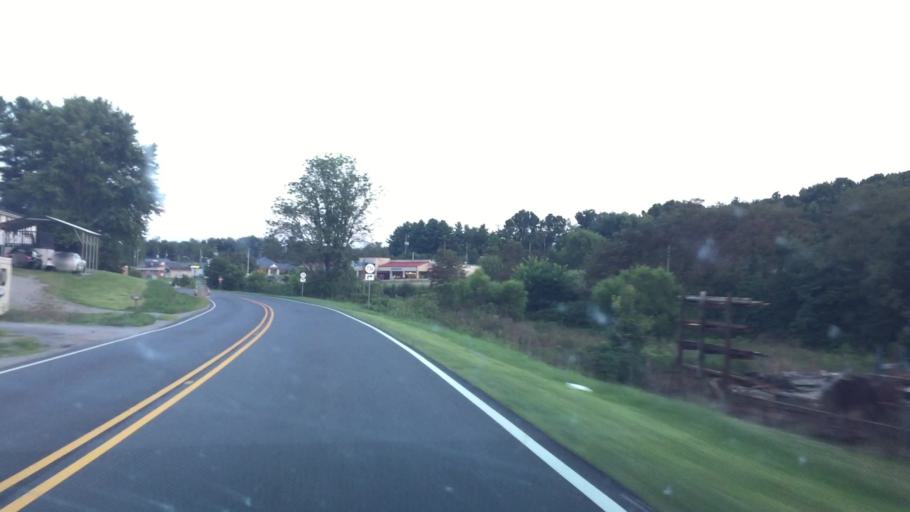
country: US
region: Virginia
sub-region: Wythe County
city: Wytheville
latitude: 36.9329
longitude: -80.9442
